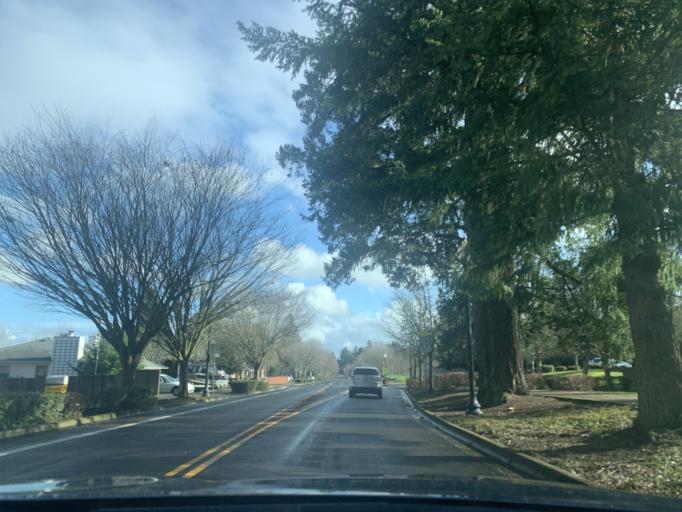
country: US
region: Oregon
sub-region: Washington County
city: Sherwood
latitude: 45.3587
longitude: -122.8548
